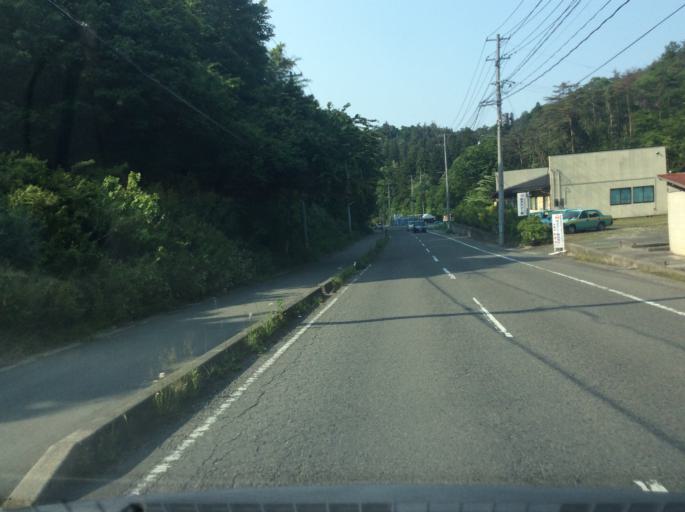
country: JP
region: Fukushima
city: Ishikawa
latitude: 37.1097
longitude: 140.2280
